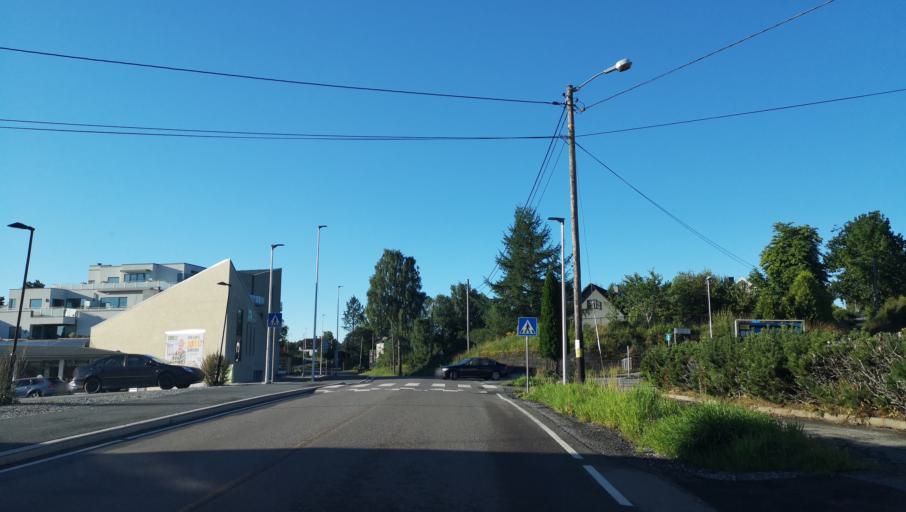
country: NO
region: Ostfold
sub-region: Hobol
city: Tomter
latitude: 59.6601
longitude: 11.0001
